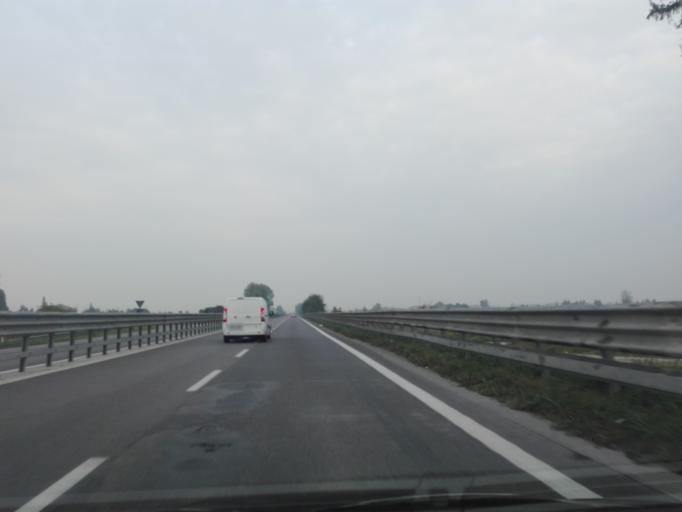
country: IT
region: Veneto
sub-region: Provincia di Rovigo
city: San Bellino
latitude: 45.0304
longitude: 11.5688
